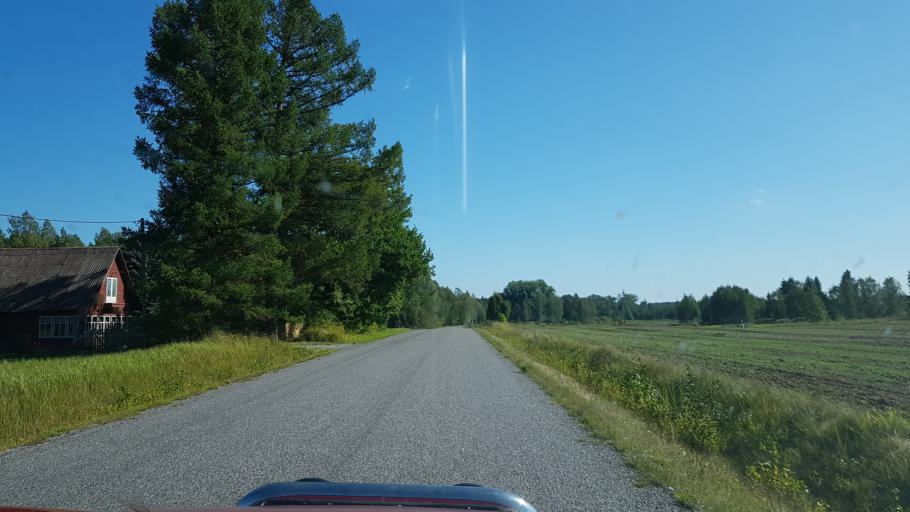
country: EE
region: Polvamaa
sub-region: Polva linn
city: Polva
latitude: 58.2116
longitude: 27.0953
